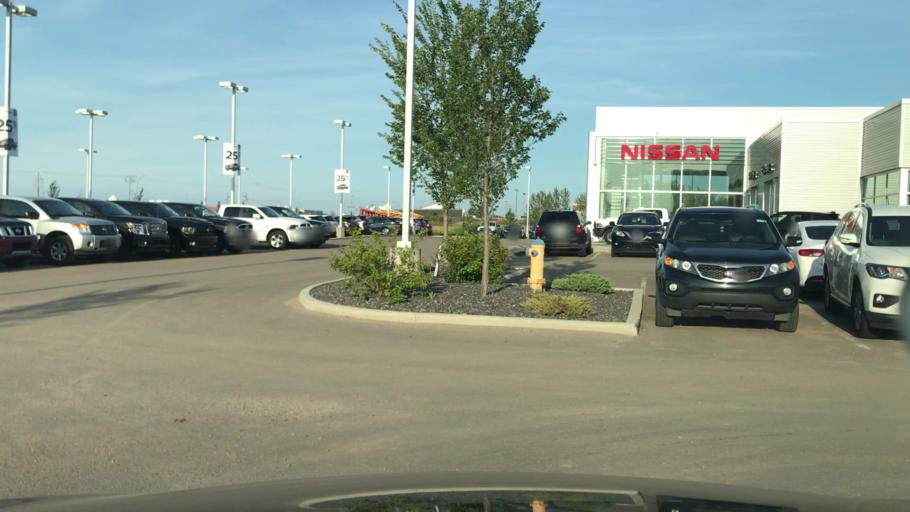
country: CA
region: Alberta
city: Leduc
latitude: 53.2787
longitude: -113.5465
